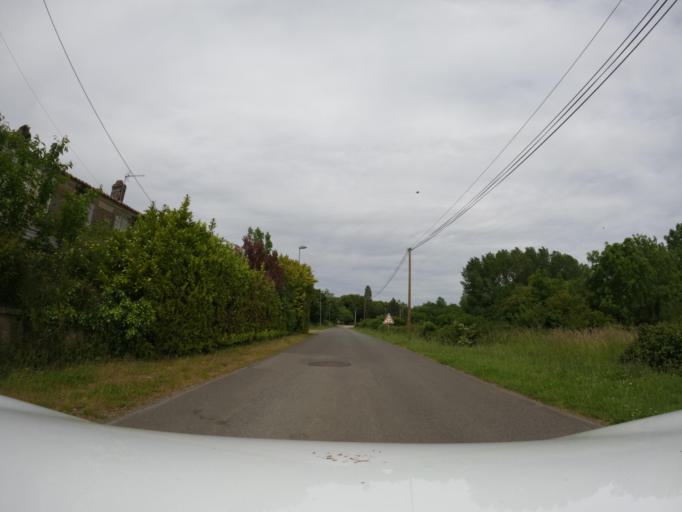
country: FR
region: Pays de la Loire
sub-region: Departement de la Vendee
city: Saint-Hilaire-des-Loges
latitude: 46.4762
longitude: -0.6597
